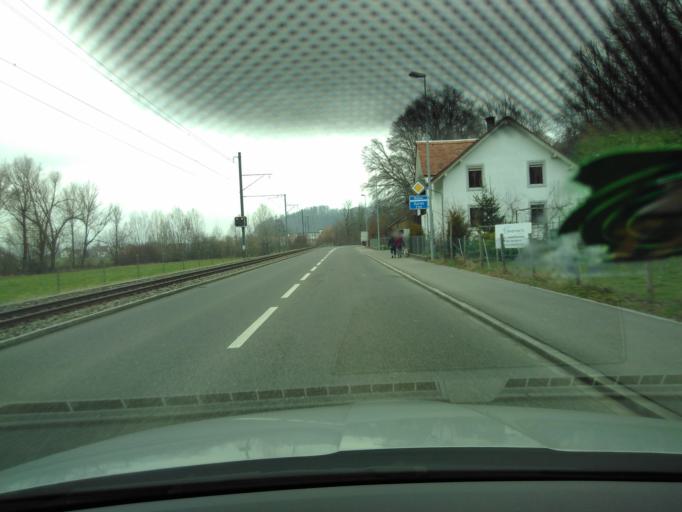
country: CH
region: Aargau
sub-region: Bezirk Aarau
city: Muhen
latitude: 47.3243
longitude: 8.0542
